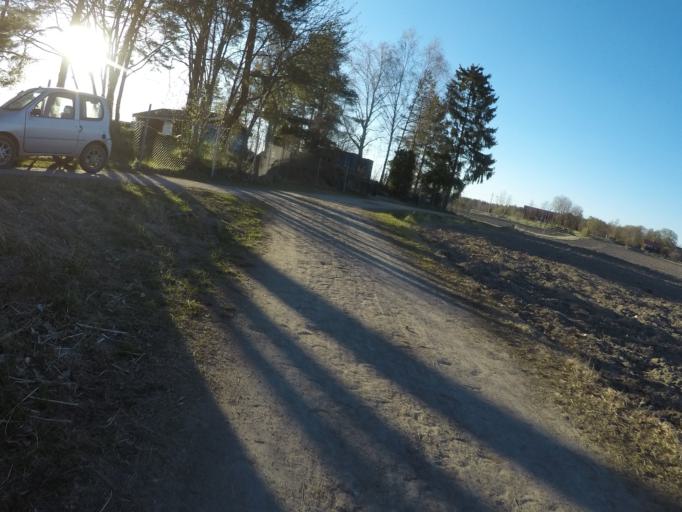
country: SE
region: Soedermanland
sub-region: Eskilstuna Kommun
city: Eskilstuna
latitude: 59.3969
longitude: 16.5278
